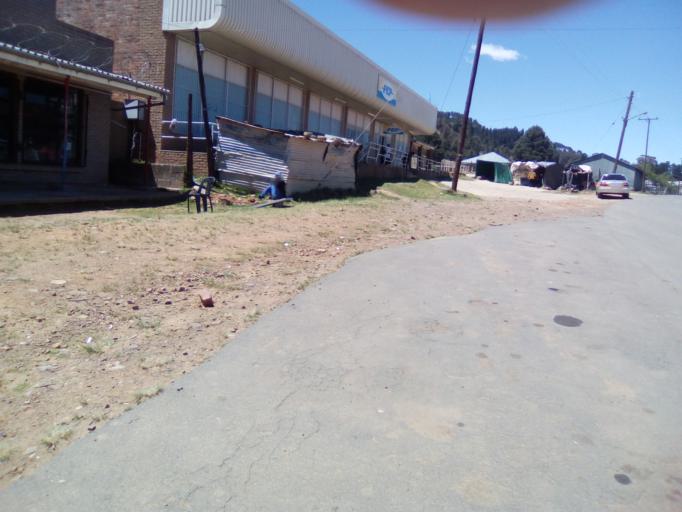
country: LS
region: Qacha's Nek
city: Qacha's Nek
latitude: -30.1169
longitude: 28.6911
